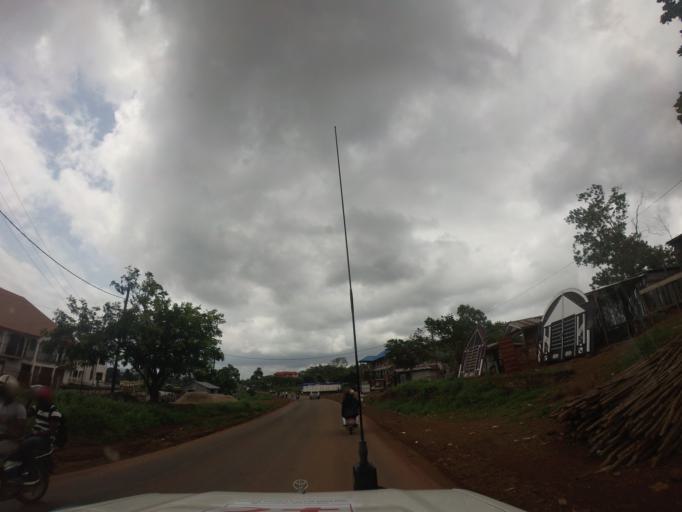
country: SL
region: Western Area
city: Hastings
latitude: 8.3812
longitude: -13.1073
